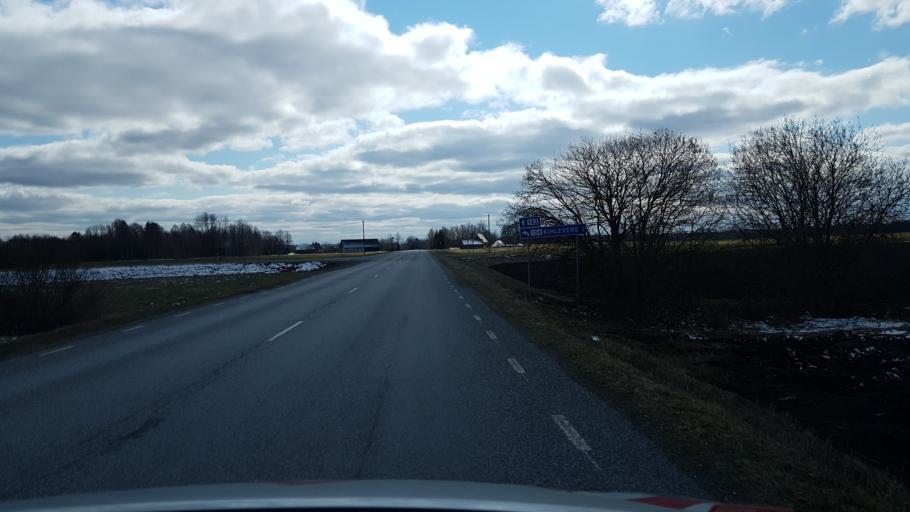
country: EE
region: Laeaene-Virumaa
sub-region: Kadrina vald
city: Kadrina
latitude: 59.3762
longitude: 26.0978
